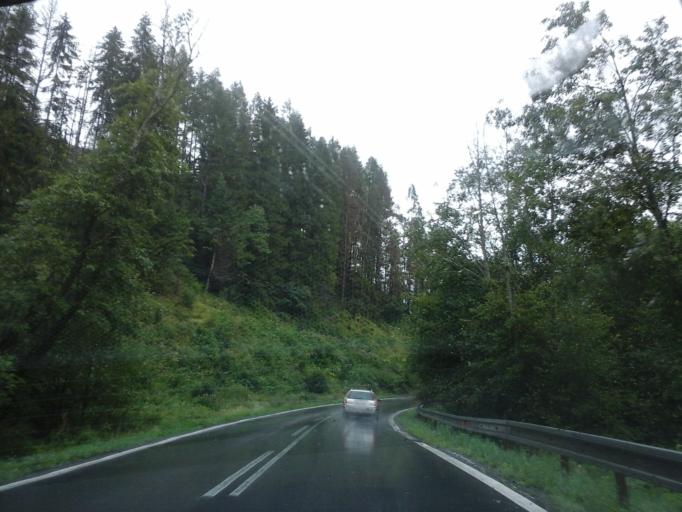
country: SK
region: Presovsky
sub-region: Okres Poprad
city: Poprad
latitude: 48.9647
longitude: 20.2927
